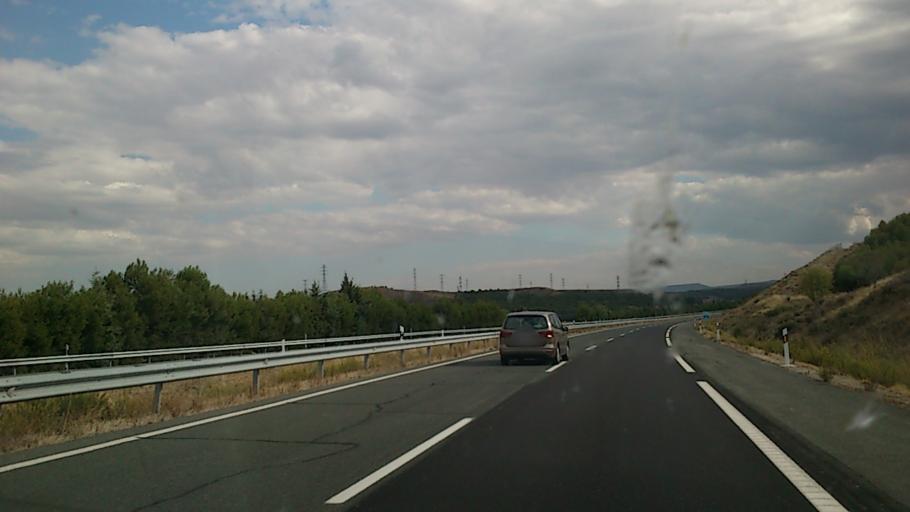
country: ES
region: La Rioja
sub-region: Provincia de La Rioja
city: Arrubal
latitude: 42.4223
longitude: -2.2666
